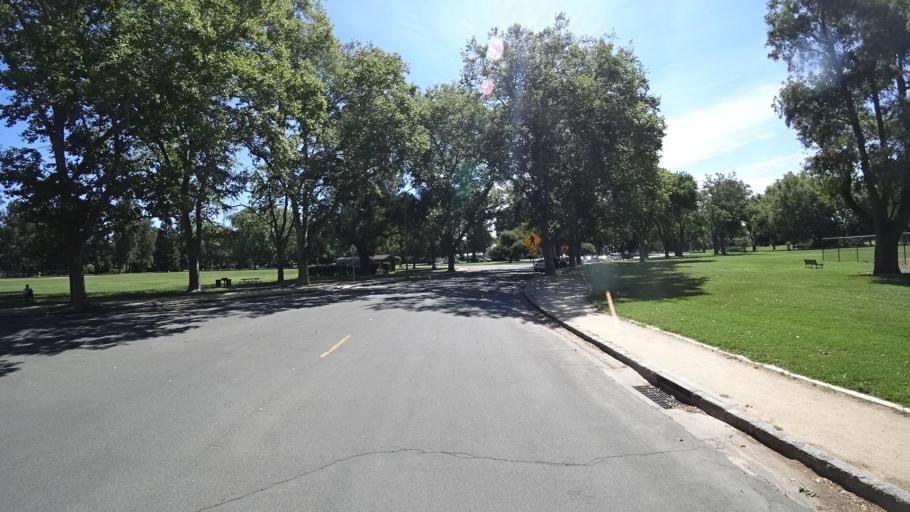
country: US
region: California
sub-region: Sacramento County
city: Sacramento
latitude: 38.5442
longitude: -121.5026
